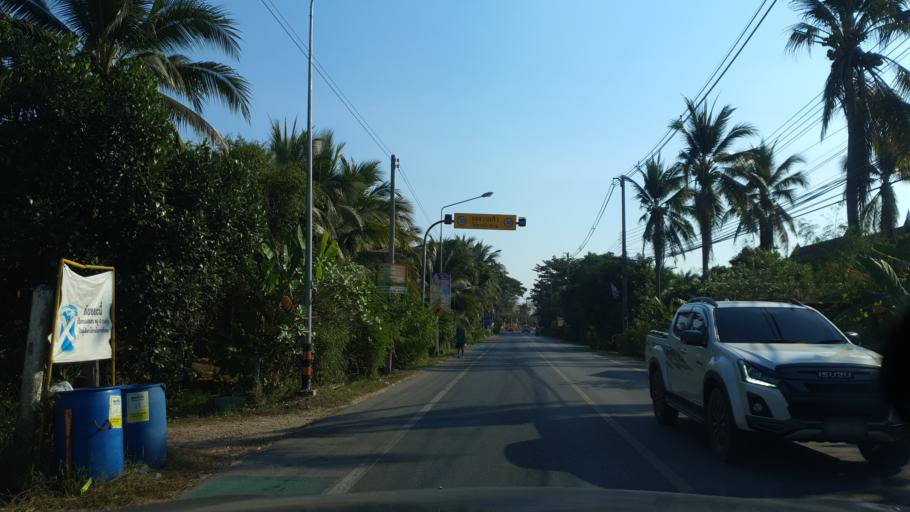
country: TH
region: Samut Songkhram
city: Bang Khon Thi
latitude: 13.4482
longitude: 99.9417
